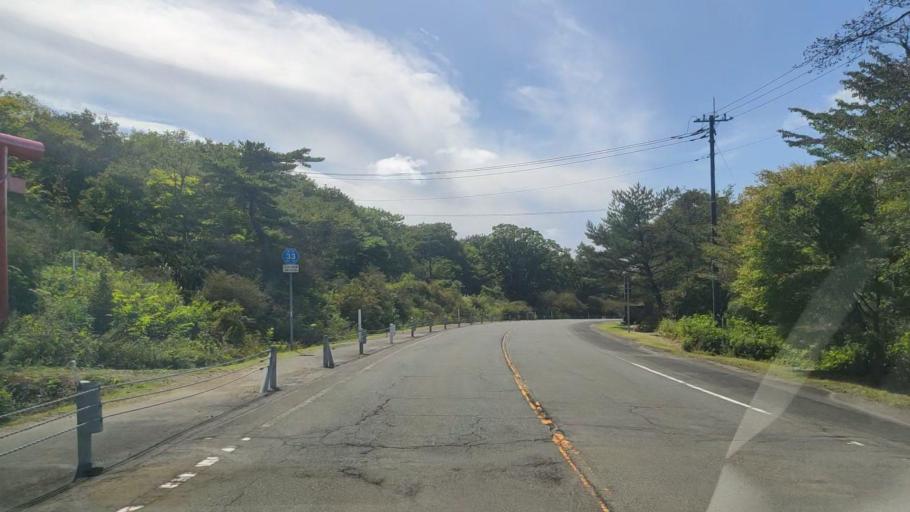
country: JP
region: Gunma
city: Shibukawa
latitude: 36.4818
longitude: 138.8962
